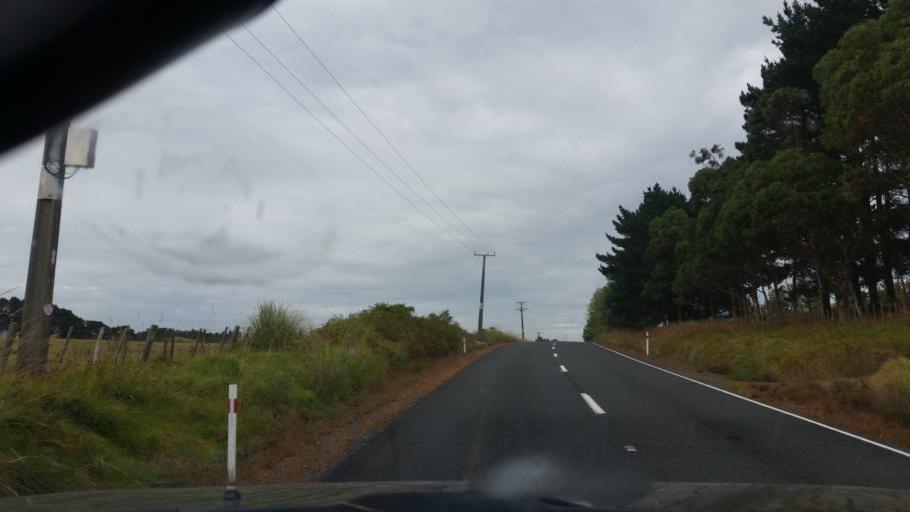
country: NZ
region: Northland
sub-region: Whangarei
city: Maungatapere
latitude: -35.8334
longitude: 174.0374
